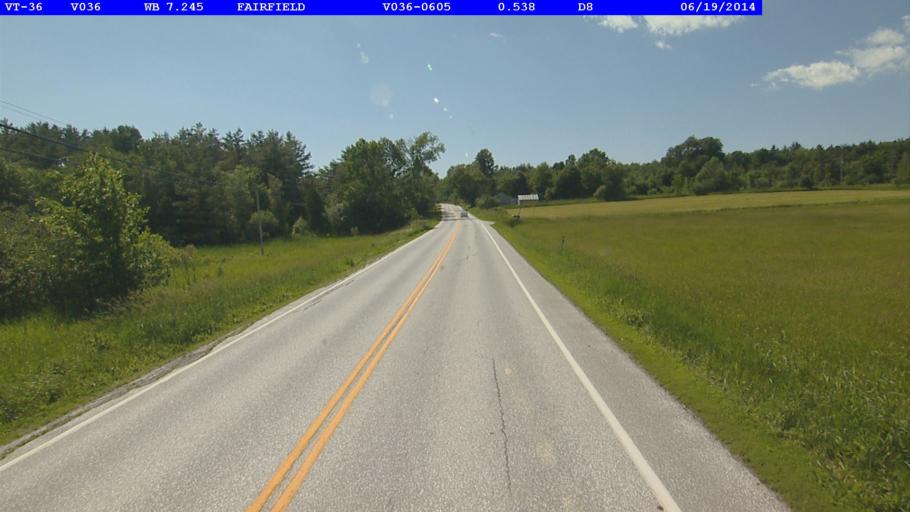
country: US
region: Vermont
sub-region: Franklin County
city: Saint Albans
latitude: 44.7892
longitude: -73.0211
